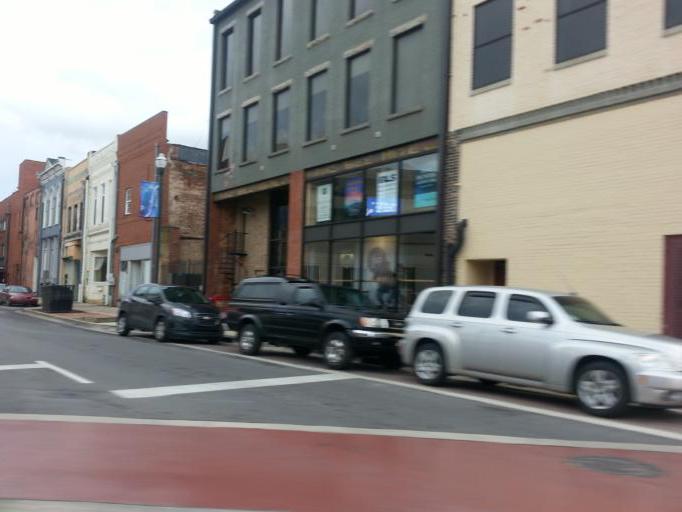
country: US
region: Tennessee
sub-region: Washington County
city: Johnson City
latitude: 36.3170
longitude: -82.3527
